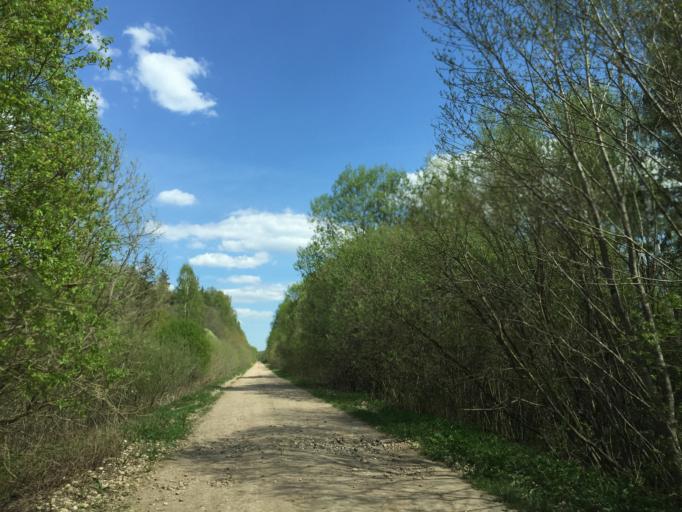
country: LV
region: Limbazu Rajons
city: Limbazi
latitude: 57.4051
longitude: 24.6055
